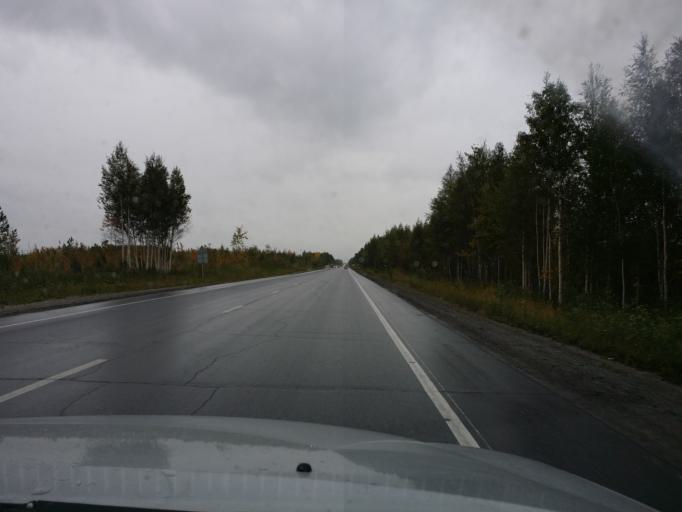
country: RU
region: Khanty-Mansiyskiy Avtonomnyy Okrug
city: Megion
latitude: 61.0675
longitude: 76.2534
